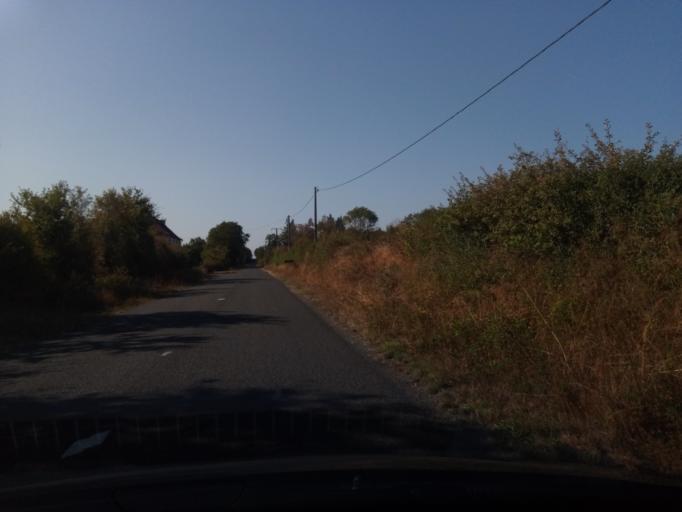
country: FR
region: Poitou-Charentes
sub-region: Departement de la Vienne
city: Saulge
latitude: 46.3695
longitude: 0.8825
